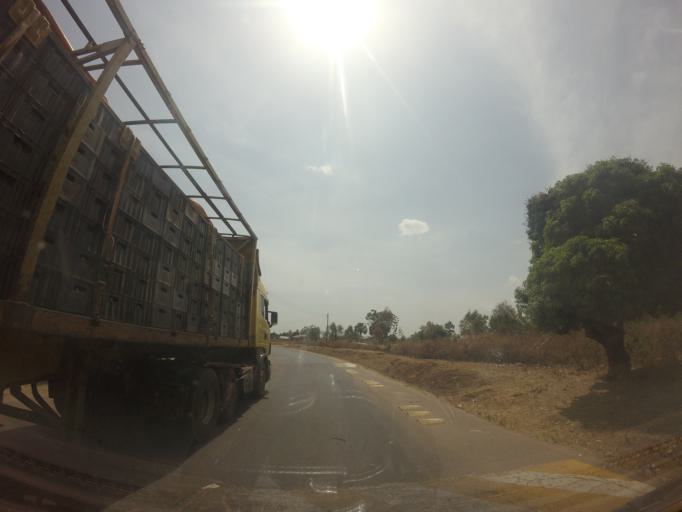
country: UG
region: Northern Region
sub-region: Arua District
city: Arua
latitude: 2.9549
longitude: 30.9172
